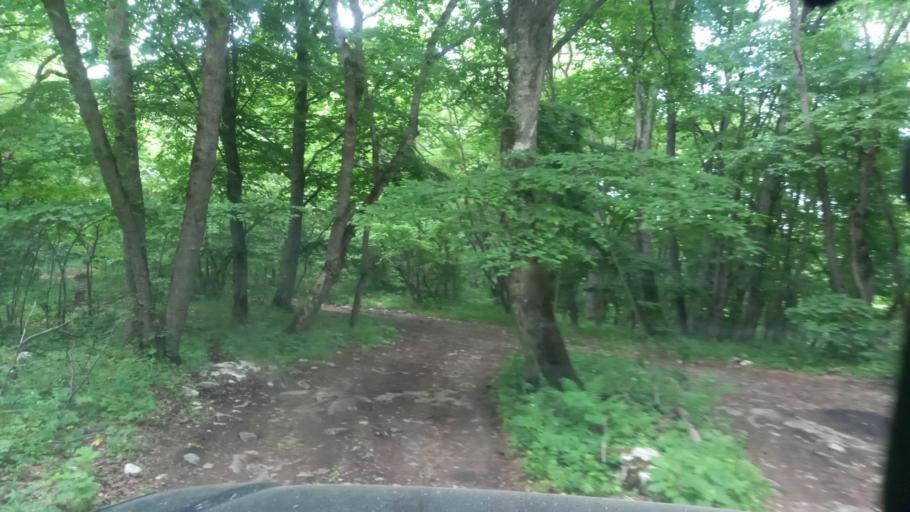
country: RU
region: Karachayevo-Cherkesiya
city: Pregradnaya
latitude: 44.0122
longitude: 41.2804
